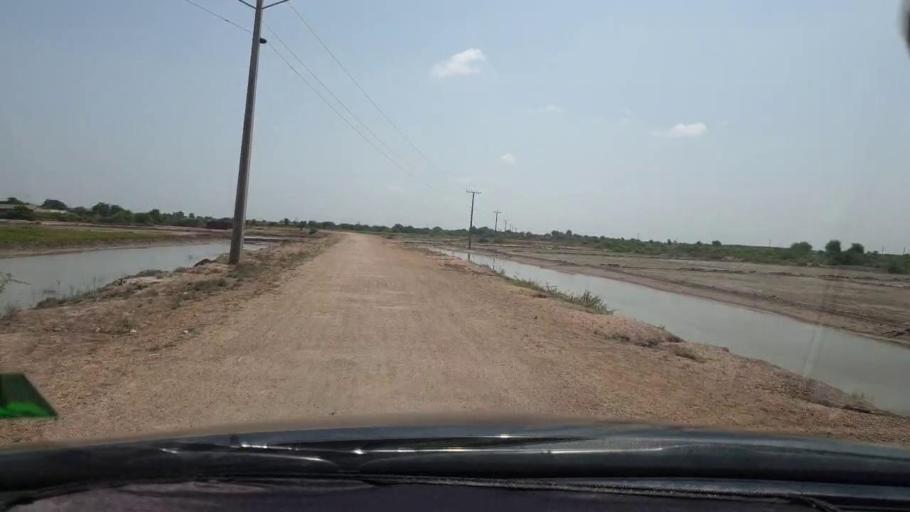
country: PK
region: Sindh
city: Tando Bago
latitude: 24.8910
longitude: 69.0989
